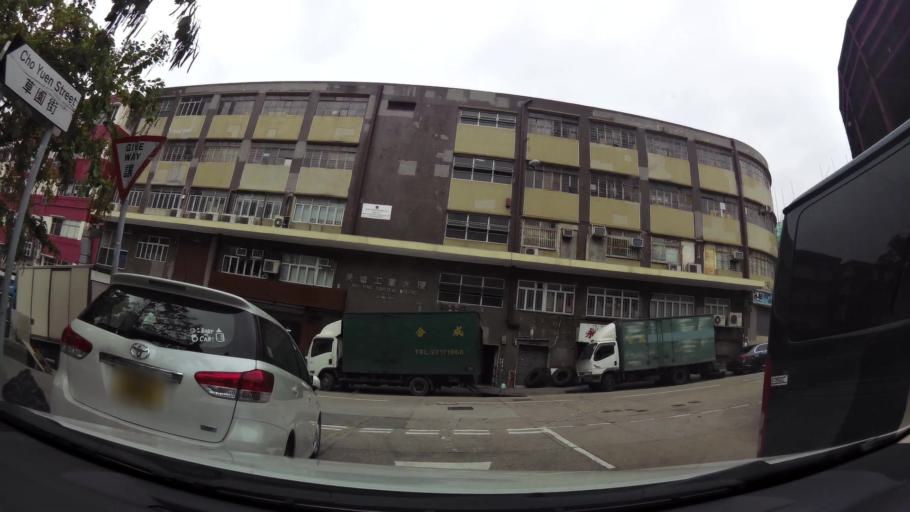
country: HK
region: Kowloon City
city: Kowloon
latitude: 22.2931
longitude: 114.2367
